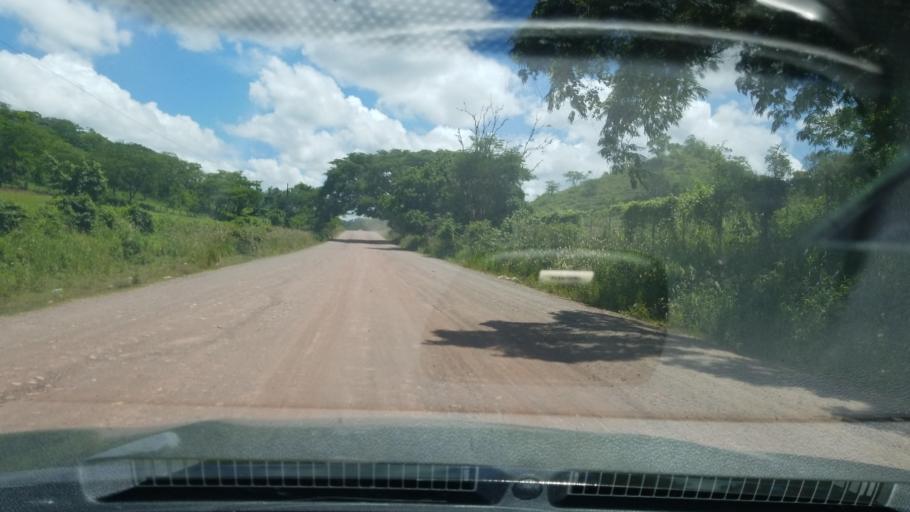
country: HN
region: Francisco Morazan
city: San Juan de Flores
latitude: 14.3248
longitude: -87.0468
